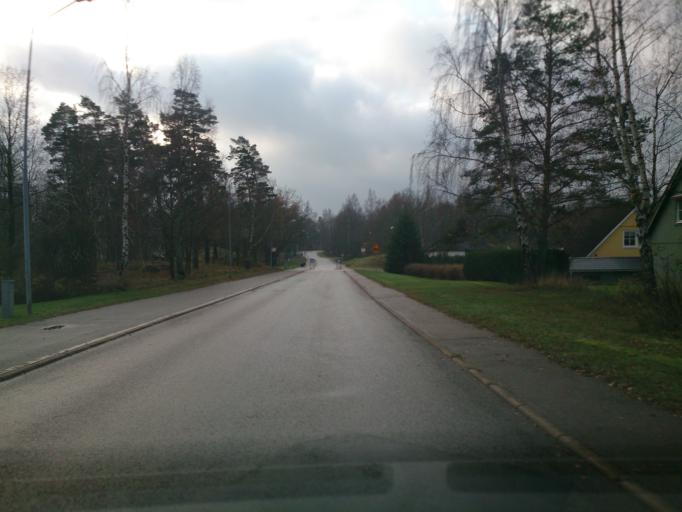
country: SE
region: OEstergoetland
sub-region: Atvidabergs Kommun
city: Atvidaberg
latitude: 58.2002
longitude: 15.9855
